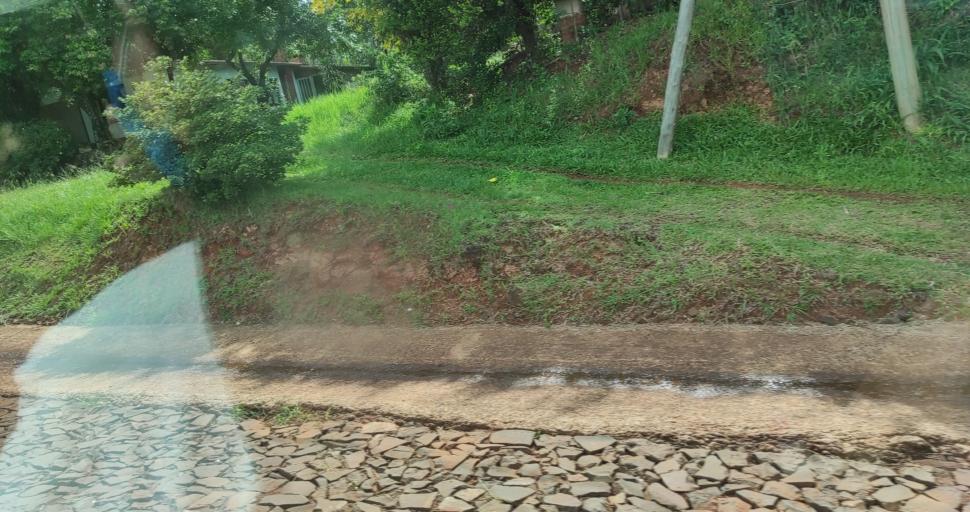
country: AR
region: Misiones
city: Dos de Mayo
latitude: -27.0327
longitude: -54.6856
